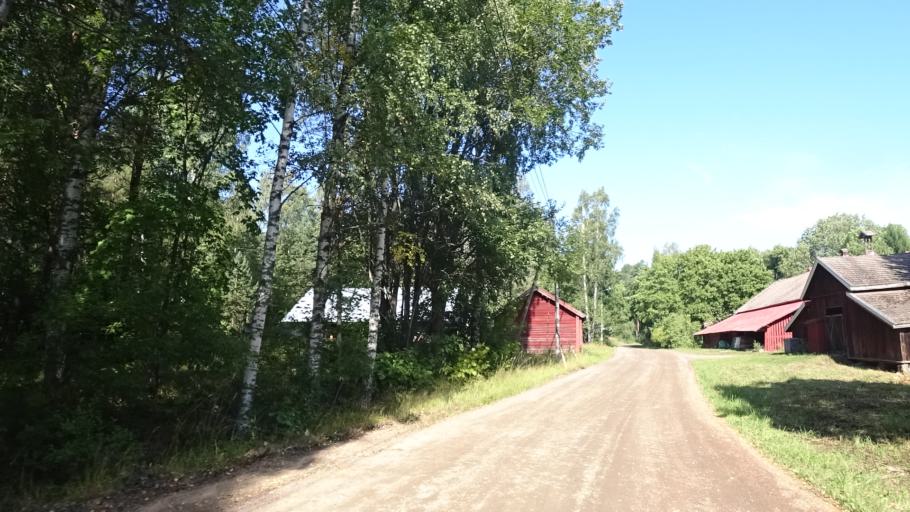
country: FI
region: Kymenlaakso
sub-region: Kotka-Hamina
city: Hamina
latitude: 60.5403
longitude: 27.2200
